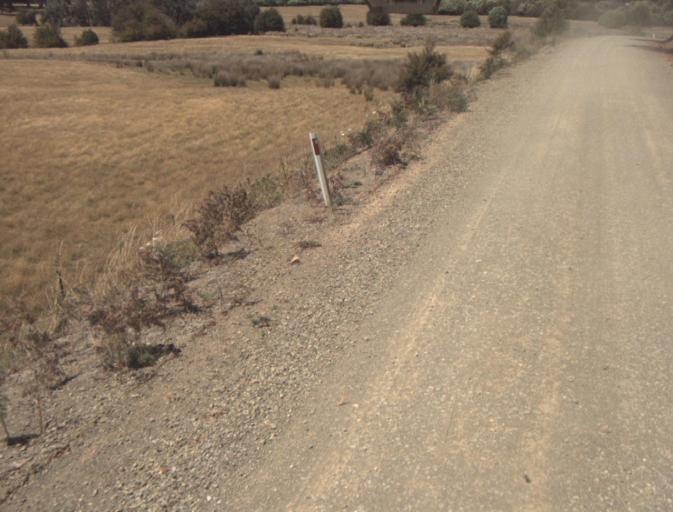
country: AU
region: Tasmania
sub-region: Dorset
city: Scottsdale
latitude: -41.3061
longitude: 147.3684
